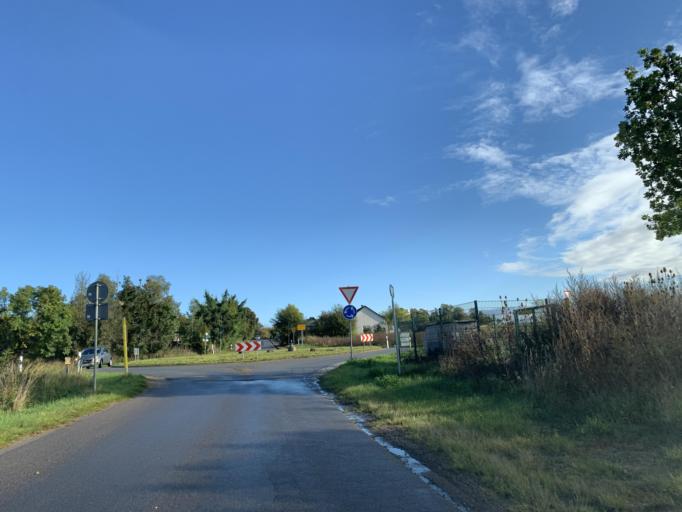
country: DE
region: Mecklenburg-Vorpommern
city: Burg Stargard
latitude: 53.4542
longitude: 13.2846
